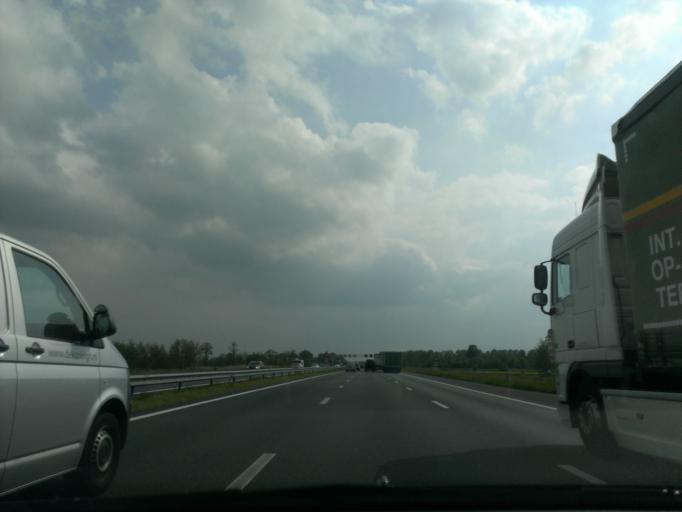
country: NL
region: Overijssel
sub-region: Gemeente Staphorst
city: Staphorst
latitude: 52.6050
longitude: 6.2057
